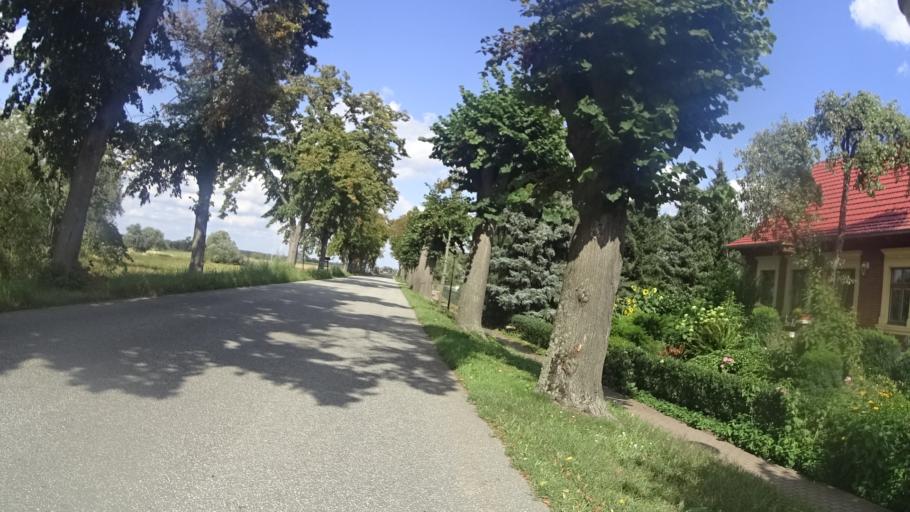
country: DE
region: Saxony-Anhalt
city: Schollene
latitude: 52.7652
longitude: 12.2336
